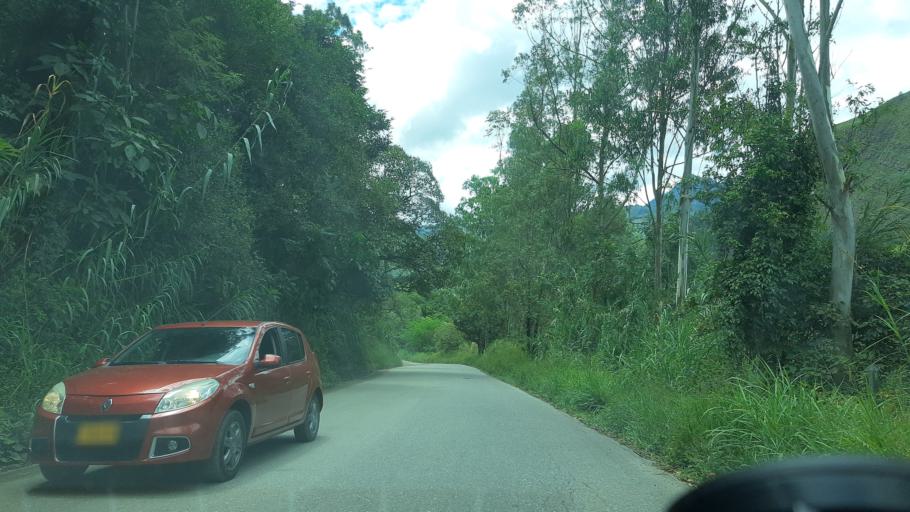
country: CO
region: Cundinamarca
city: Tenza
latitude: 5.0269
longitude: -73.3892
